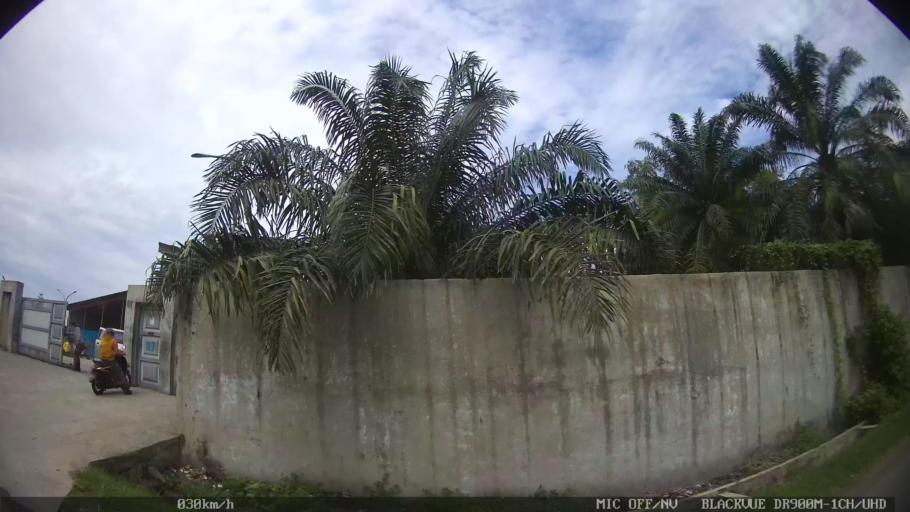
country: ID
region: North Sumatra
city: Sunggal
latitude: 3.5847
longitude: 98.5774
